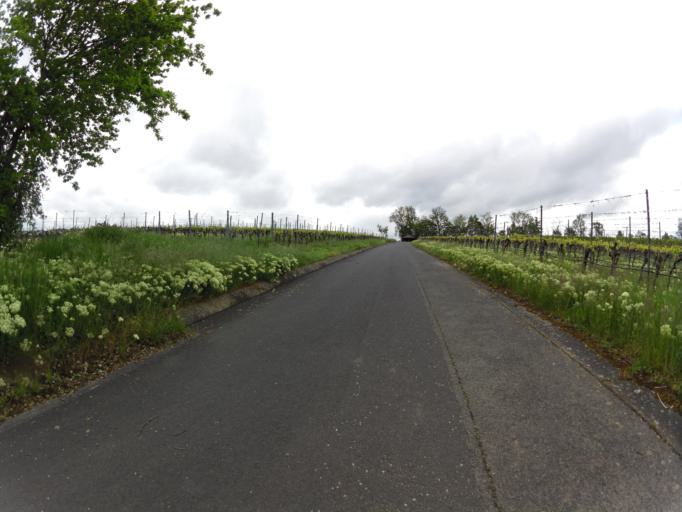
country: DE
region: Bavaria
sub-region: Regierungsbezirk Unterfranken
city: Sommerach
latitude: 49.8364
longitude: 10.2191
